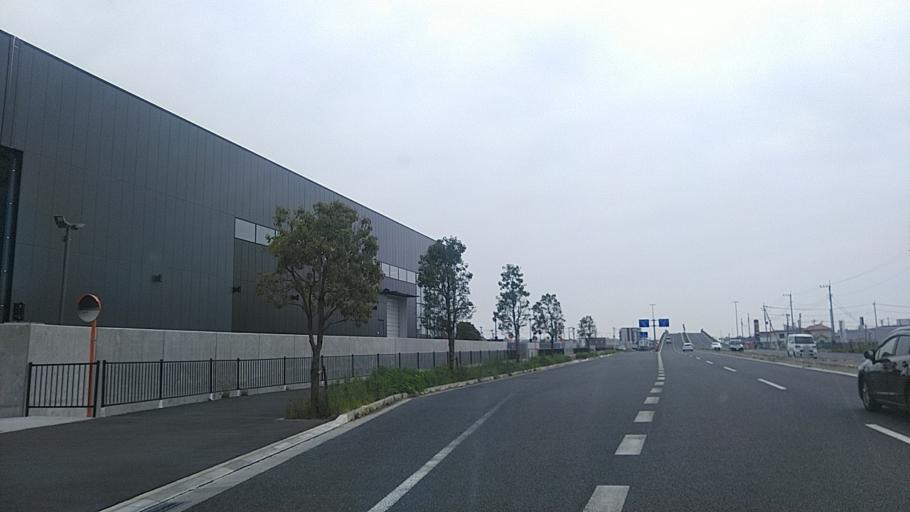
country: JP
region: Gunma
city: Ota
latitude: 36.2695
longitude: 139.3728
